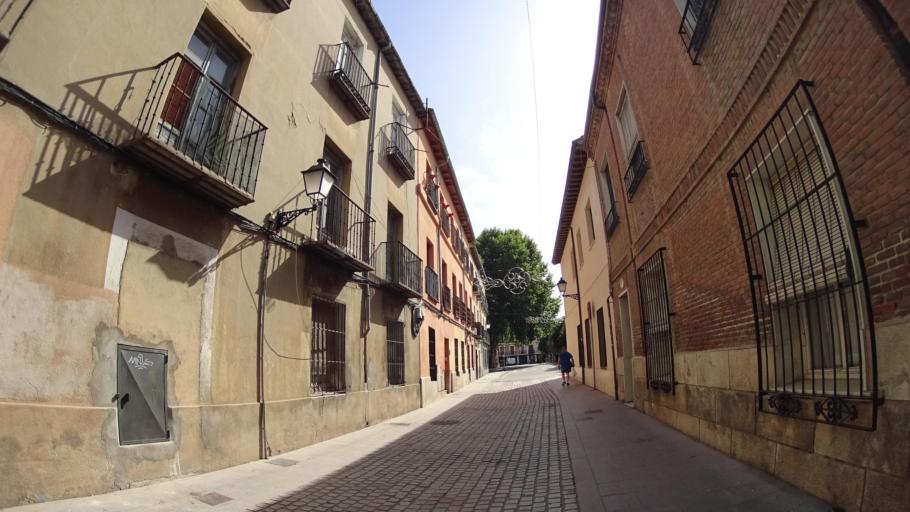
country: ES
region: Madrid
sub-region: Provincia de Madrid
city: Alcala de Henares
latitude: 40.4809
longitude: -3.3701
